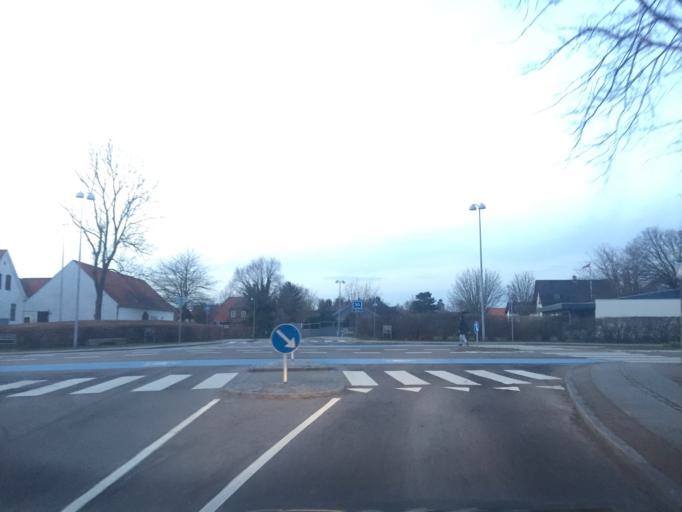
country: DK
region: Capital Region
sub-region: Hoje-Taastrup Kommune
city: Taastrup
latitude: 55.6428
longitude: 12.3087
